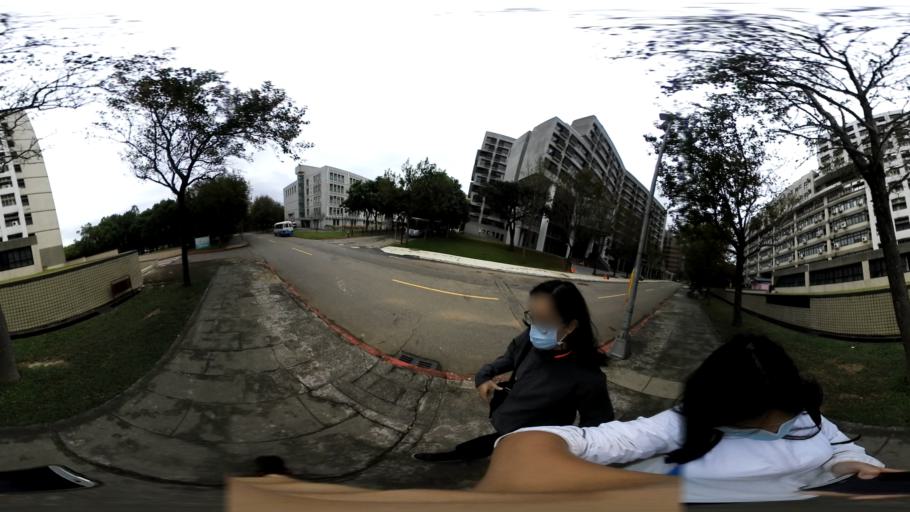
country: TW
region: Taiwan
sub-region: Hsinchu
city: Hsinchu
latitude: 24.7843
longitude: 120.9972
